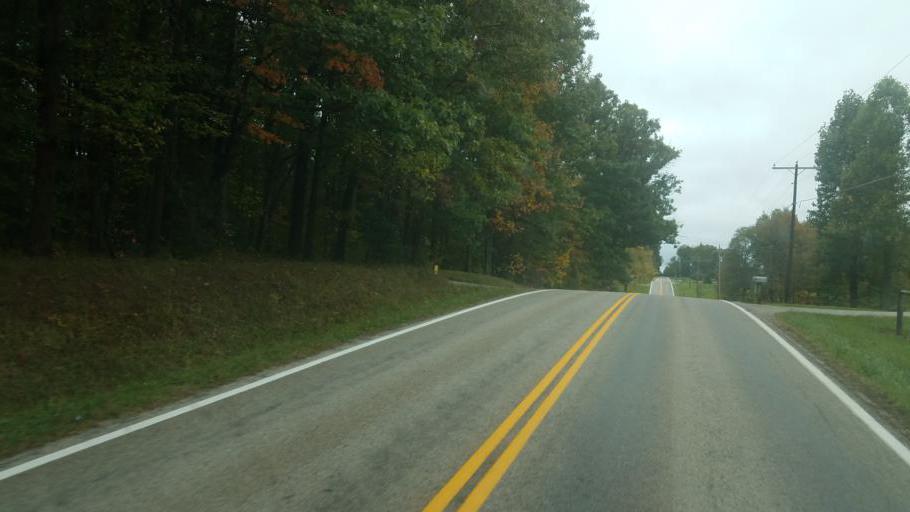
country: US
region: Ohio
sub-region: Ashland County
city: Ashland
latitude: 40.7949
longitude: -82.3397
